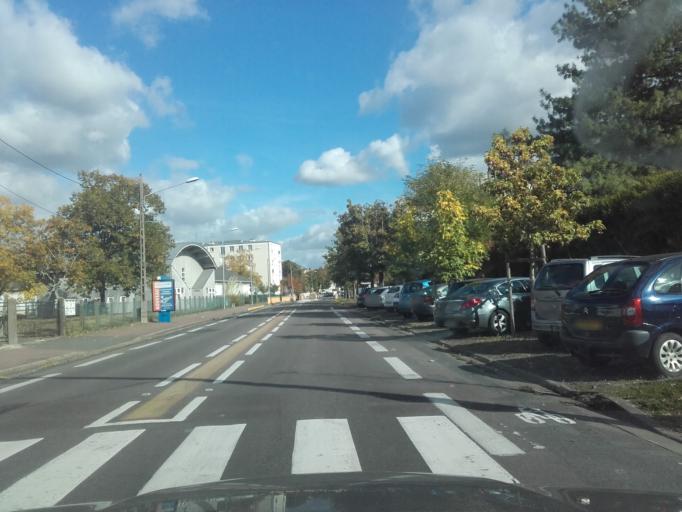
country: FR
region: Centre
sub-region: Departement d'Indre-et-Loire
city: Saint-Pierre-des-Corps
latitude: 47.3887
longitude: 0.7296
